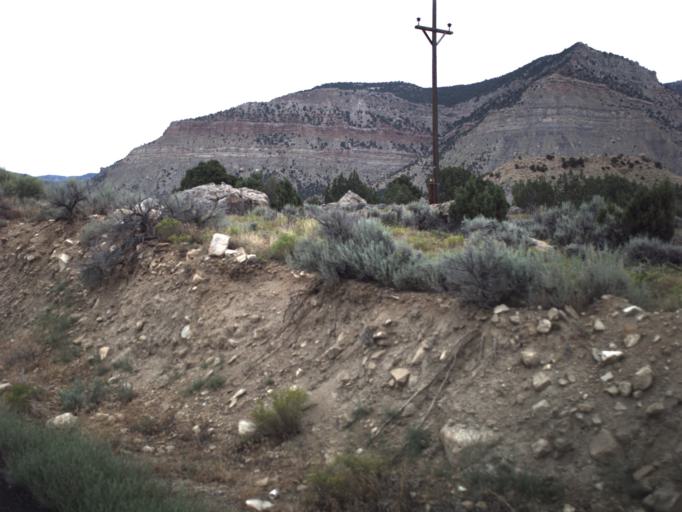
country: US
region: Utah
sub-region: Carbon County
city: East Carbon City
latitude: 39.5146
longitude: -110.3927
